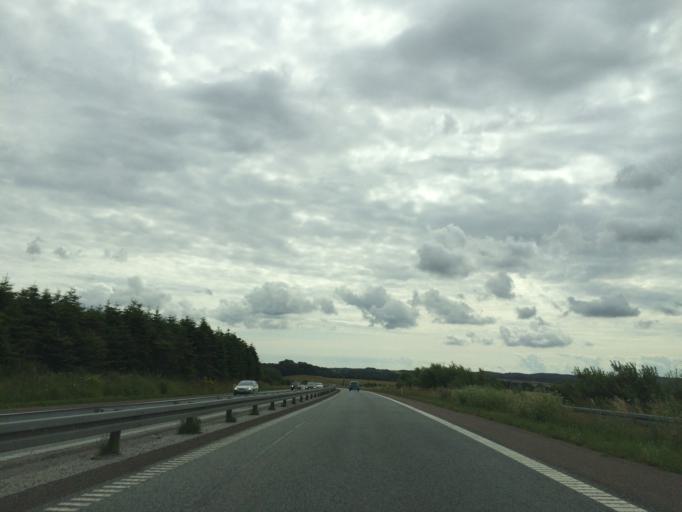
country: DK
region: Central Jutland
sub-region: Syddjurs Kommune
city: Ronde
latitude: 56.2964
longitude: 10.5207
